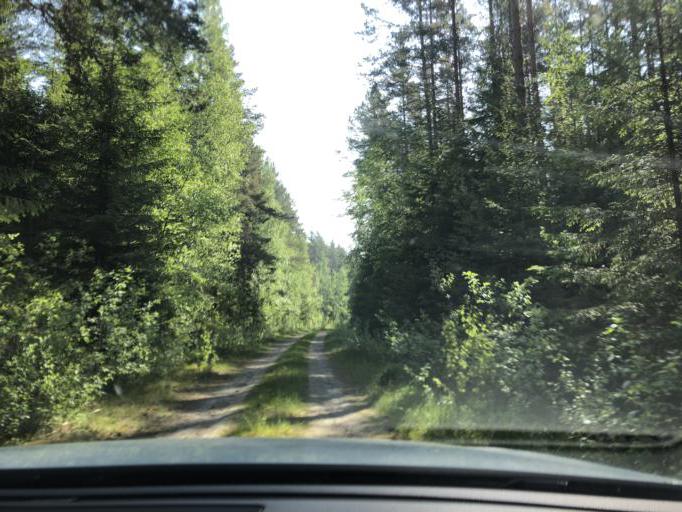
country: SE
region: Dalarna
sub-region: Avesta Kommun
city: Horndal
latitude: 60.2161
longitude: 16.5015
